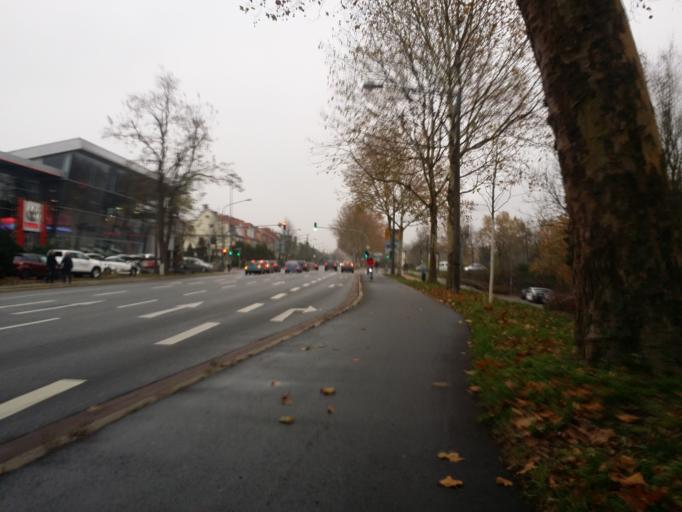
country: DE
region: Bremen
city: Bremen
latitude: 53.0651
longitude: 8.8521
